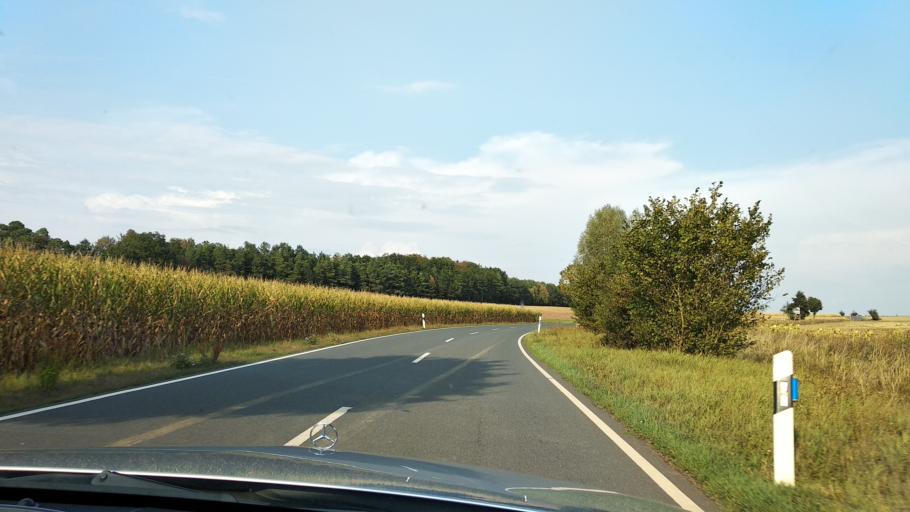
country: DE
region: Baden-Wuerttemberg
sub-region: Karlsruhe Region
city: Hopfingen
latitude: 49.5940
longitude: 9.4007
